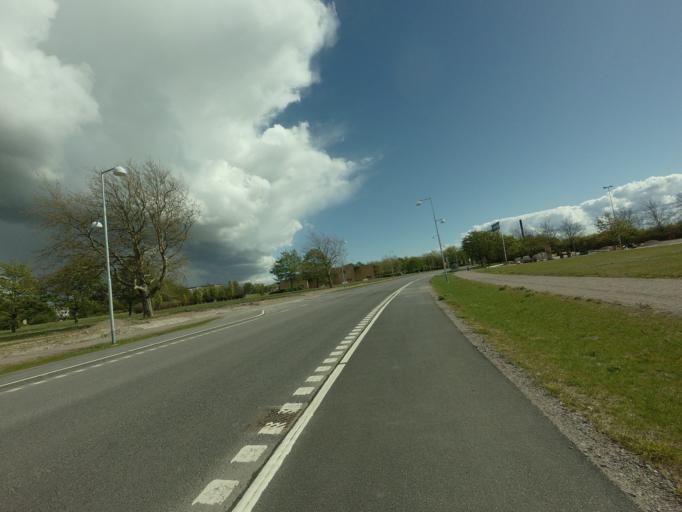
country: SE
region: Skane
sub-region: Landskrona
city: Landskrona
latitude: 55.8927
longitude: 12.8437
